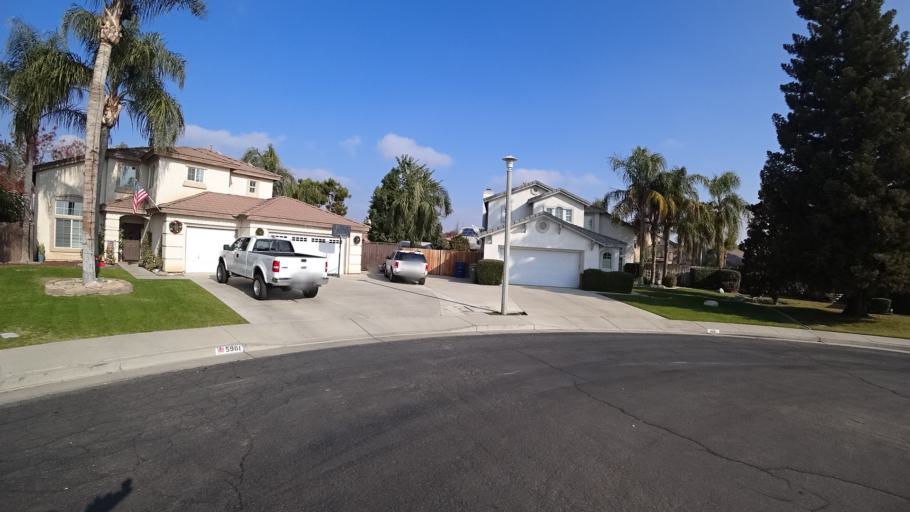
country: US
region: California
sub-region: Kern County
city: Greenacres
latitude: 35.3016
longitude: -119.0848
